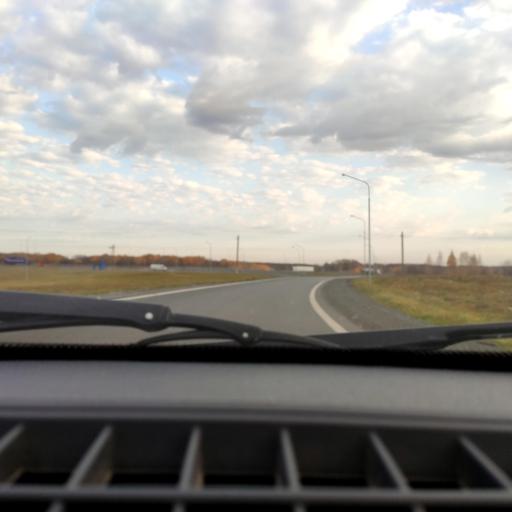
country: RU
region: Bashkortostan
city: Avdon
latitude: 54.6624
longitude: 55.7360
